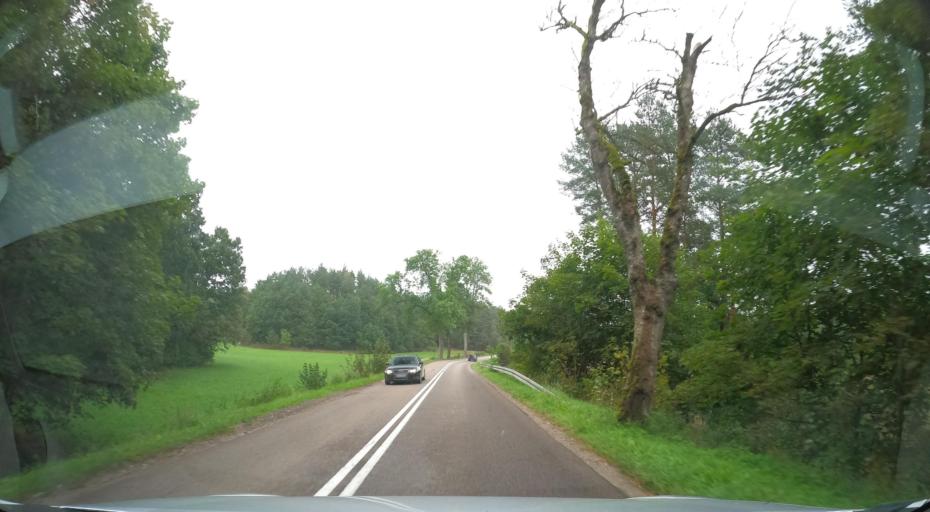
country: PL
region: Pomeranian Voivodeship
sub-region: Powiat wejherowski
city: Luzino
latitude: 54.4726
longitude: 18.0807
